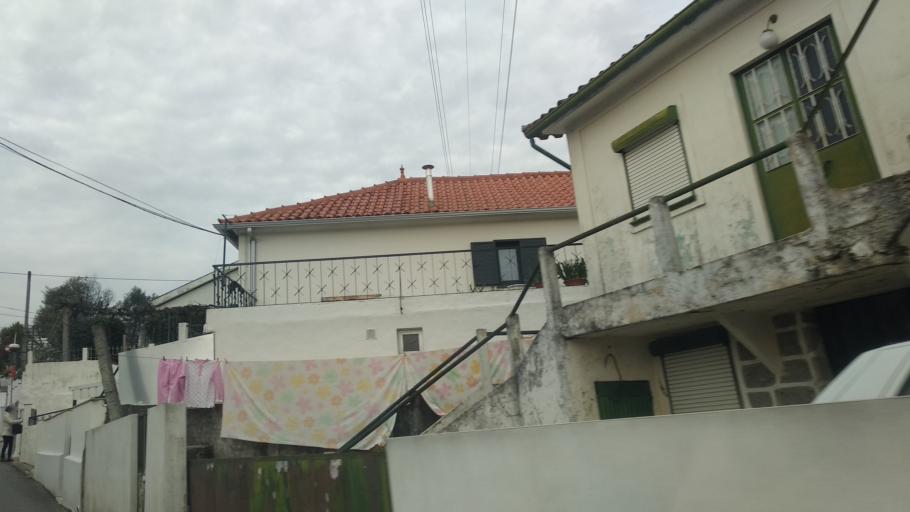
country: PT
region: Braga
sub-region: Braga
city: Braga
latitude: 41.5257
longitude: -8.4431
